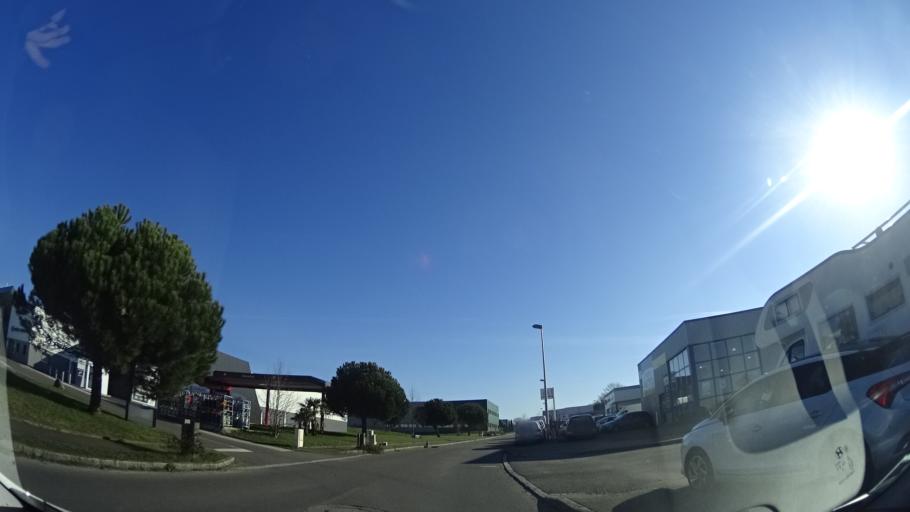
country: FR
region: Brittany
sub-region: Departement d'Ille-et-Vilaine
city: La Meziere
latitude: 48.2140
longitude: -1.7437
